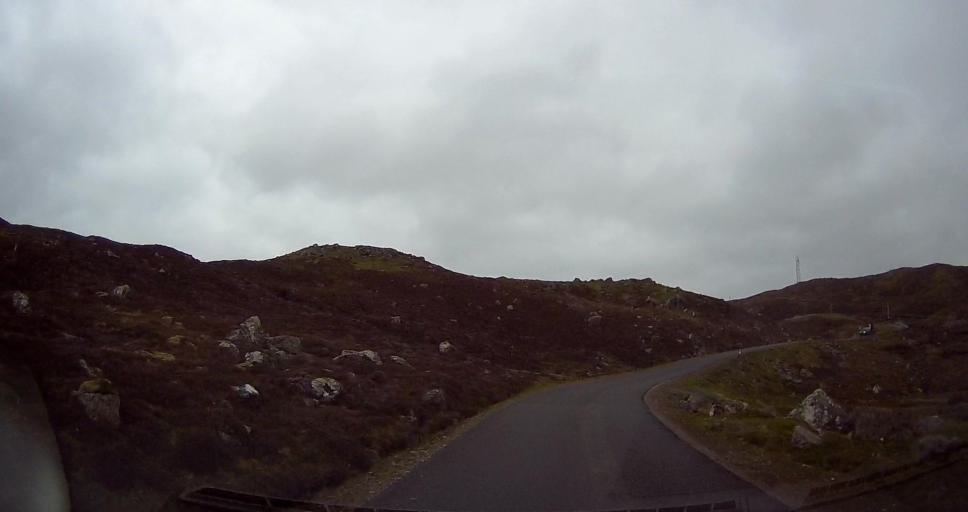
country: GB
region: Scotland
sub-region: Shetland Islands
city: Lerwick
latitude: 60.3411
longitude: -1.3121
